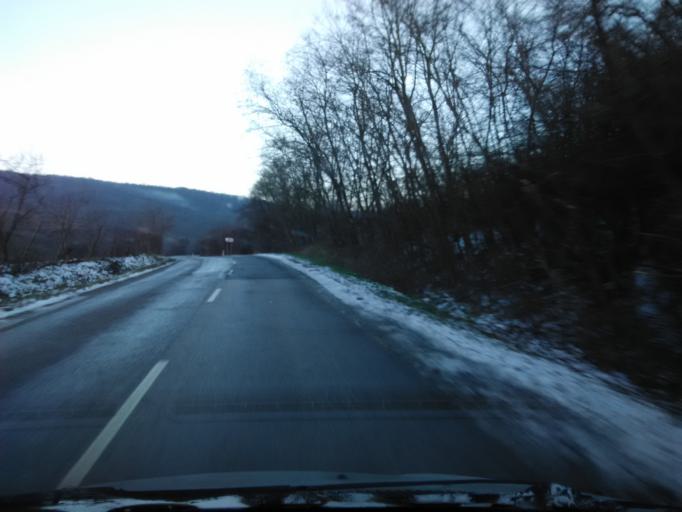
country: SK
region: Nitriansky
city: Tlmace
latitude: 48.2760
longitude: 18.5046
